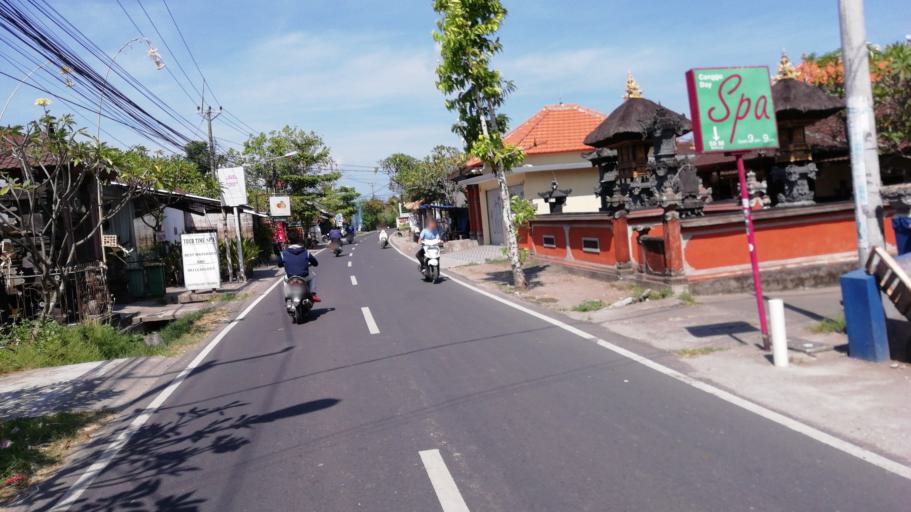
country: ID
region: Bali
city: Banjar Gunungpande
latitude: -8.6460
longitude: 115.1409
